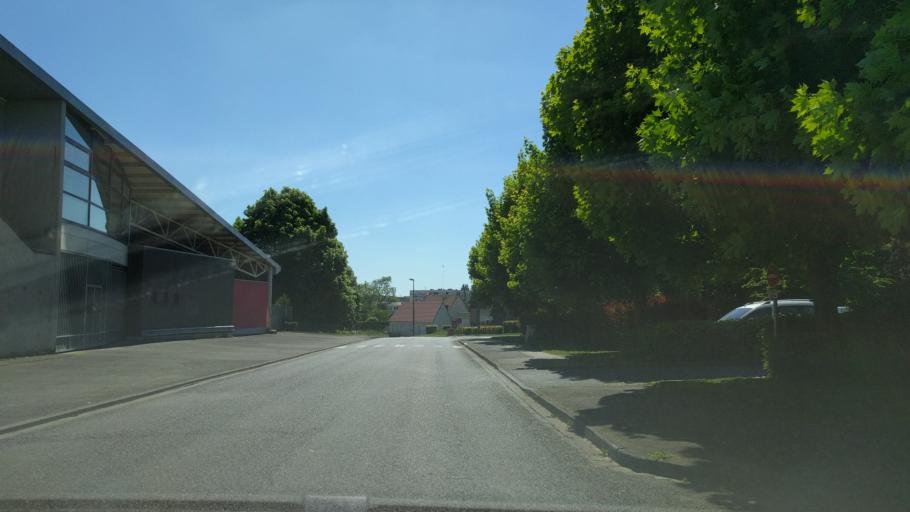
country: FR
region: Picardie
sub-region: Departement de la Somme
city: Peronne
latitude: 49.9375
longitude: 2.9409
